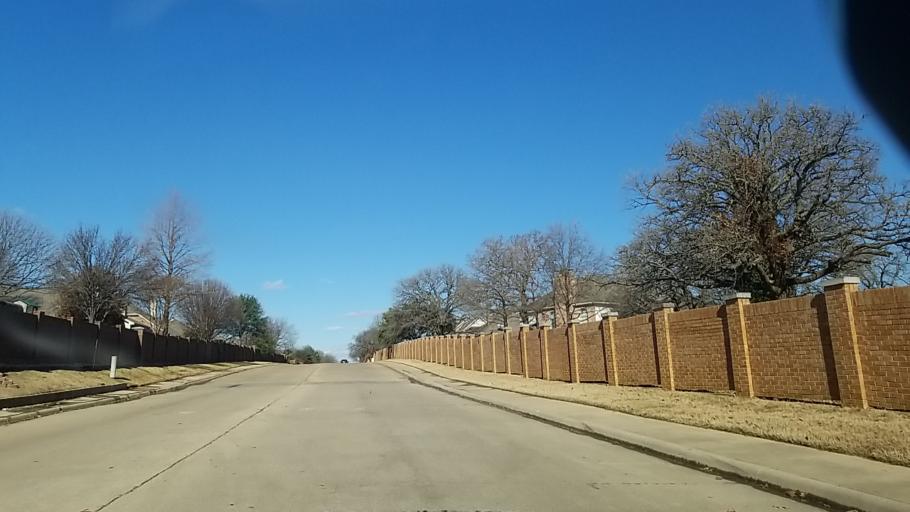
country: US
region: Texas
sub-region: Denton County
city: Corinth
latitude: 33.1596
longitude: -97.0877
